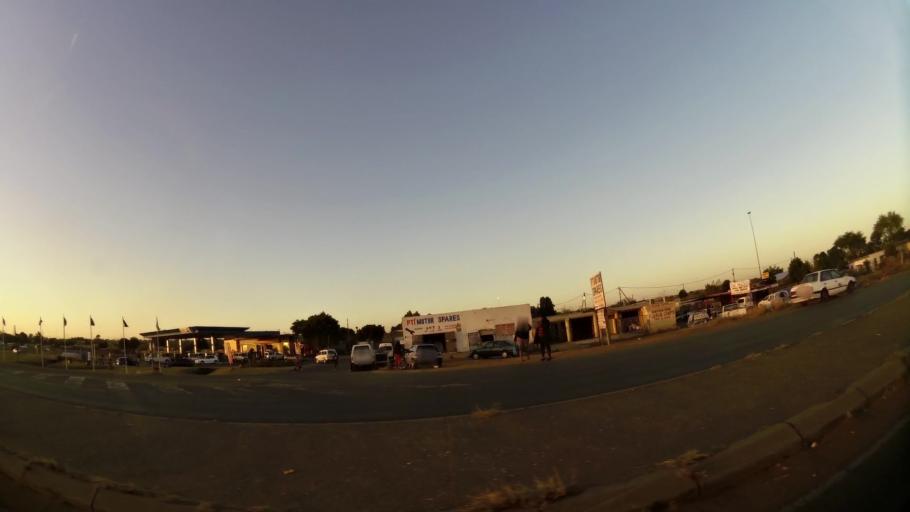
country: ZA
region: North-West
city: Ga-Rankuwa
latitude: -25.5678
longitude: 28.0573
